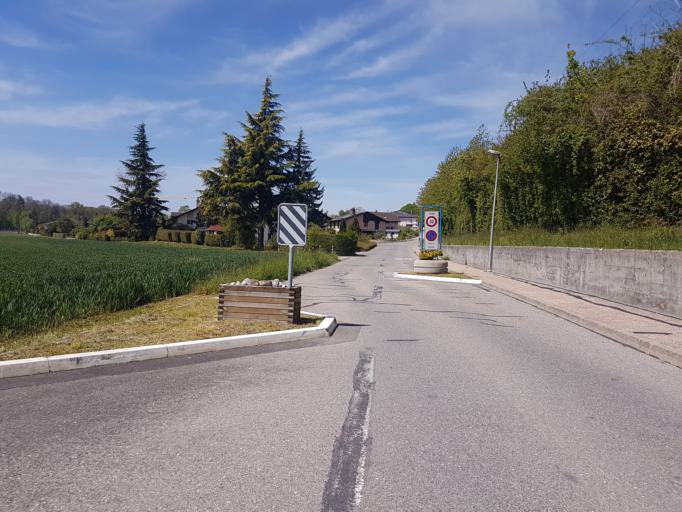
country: CH
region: Neuchatel
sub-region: Neuchatel District
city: Cornaux
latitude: 47.0091
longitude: 7.0211
